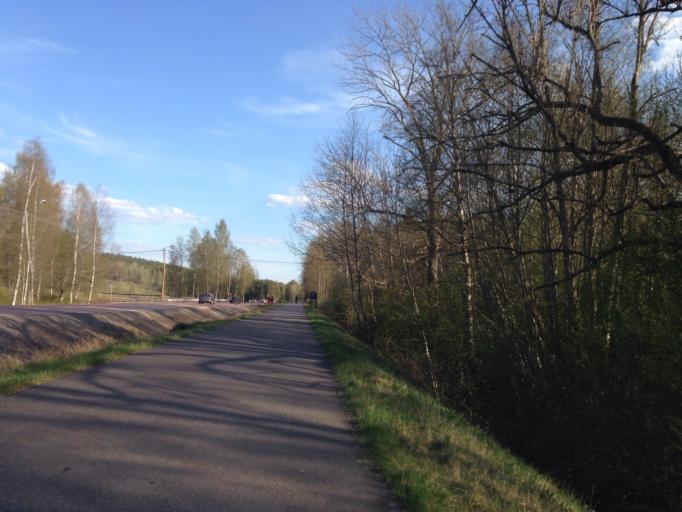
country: SE
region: Dalarna
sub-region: Ludvika Kommun
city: Ludvika
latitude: 60.1831
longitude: 15.1525
